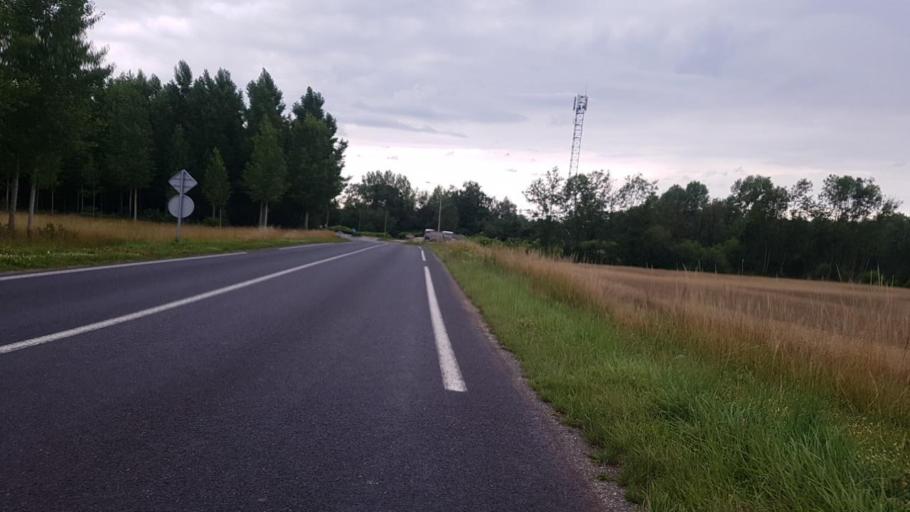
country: FR
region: Champagne-Ardenne
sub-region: Departement de la Marne
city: Vitry-le-Francois
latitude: 48.7523
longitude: 4.7070
